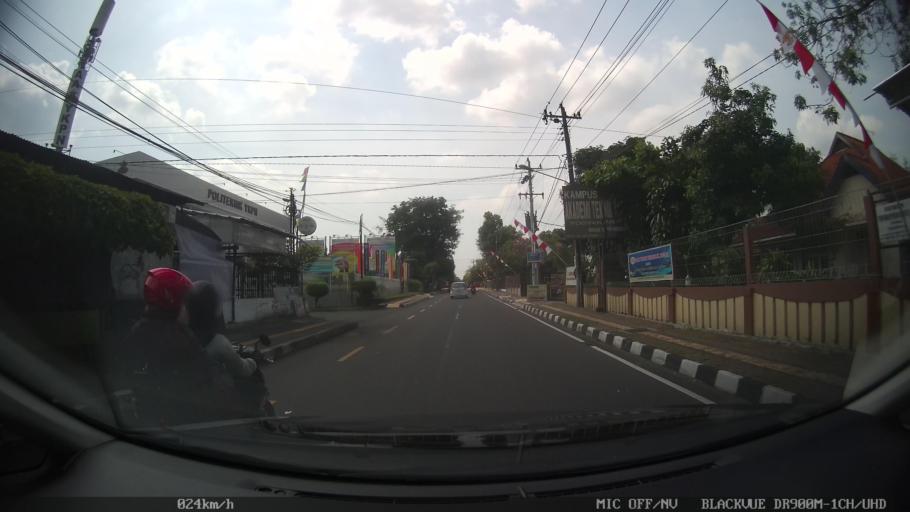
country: ID
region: Daerah Istimewa Yogyakarta
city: Yogyakarta
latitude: -7.7862
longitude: 110.3827
